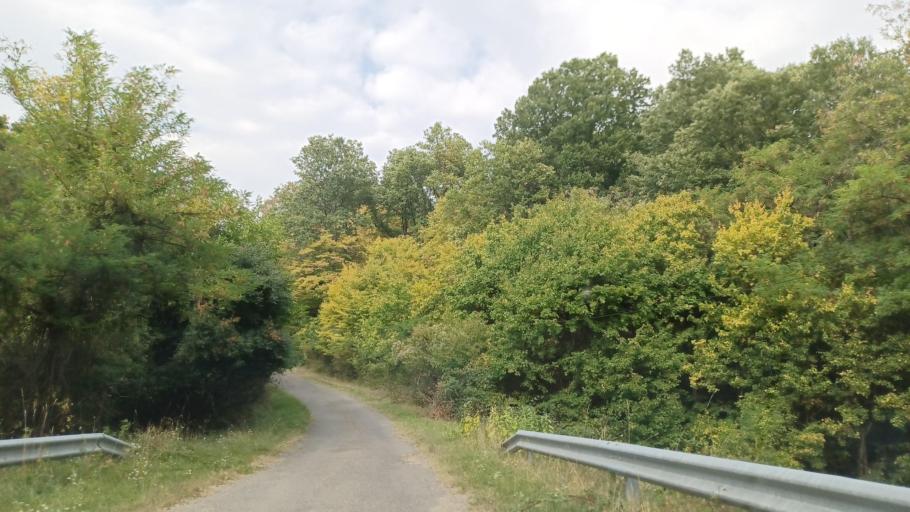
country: HU
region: Baranya
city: Mecseknadasd
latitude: 46.2022
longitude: 18.4528
